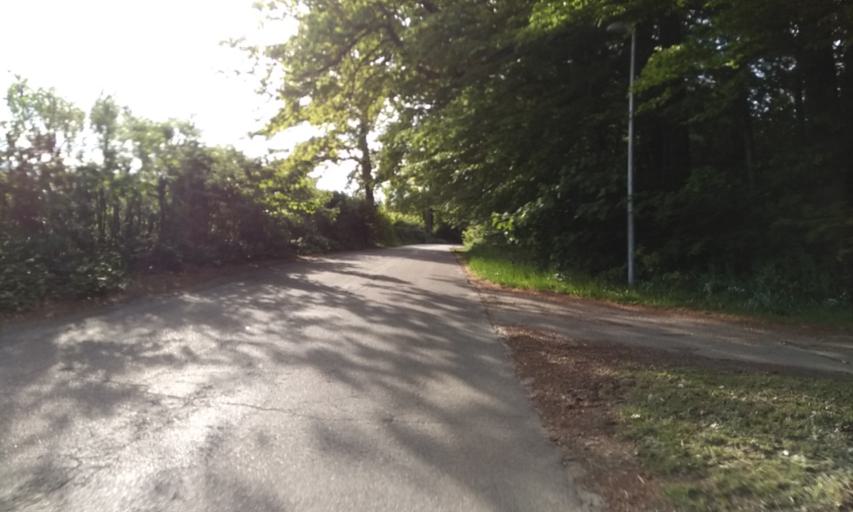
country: DE
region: Lower Saxony
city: Nottensdorf
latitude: 53.4819
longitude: 9.6050
